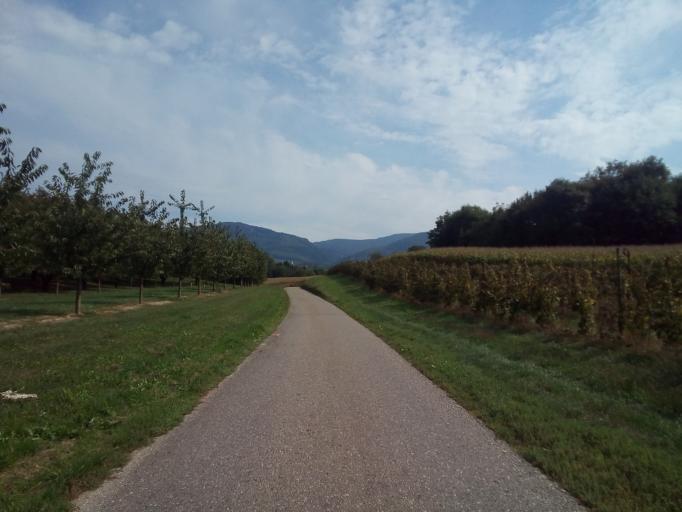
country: DE
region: Baden-Wuerttemberg
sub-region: Freiburg Region
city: Sasbach
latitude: 48.6502
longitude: 8.0985
